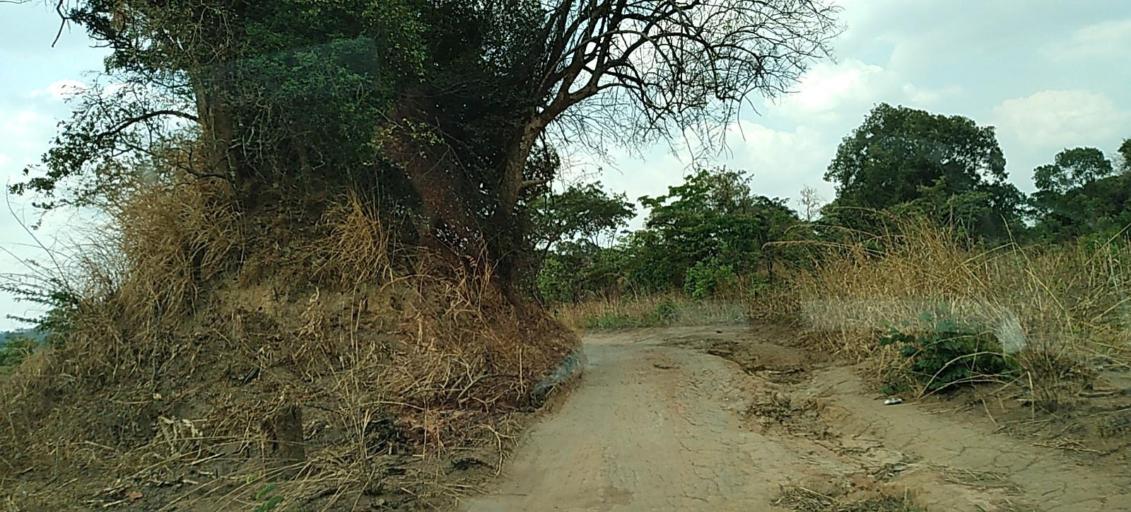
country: ZM
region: Copperbelt
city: Chililabombwe
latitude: -12.3257
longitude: 27.7485
